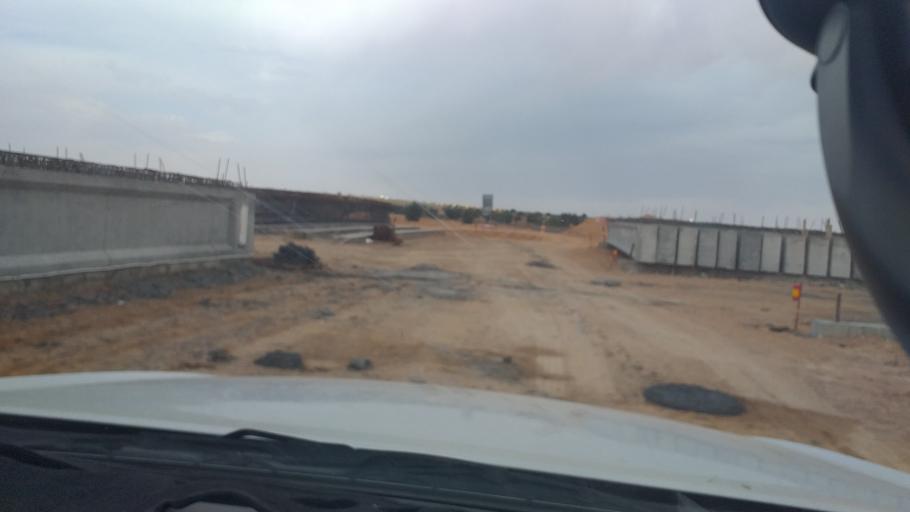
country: TN
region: Madanin
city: Medenine
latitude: 33.3182
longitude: 10.6057
